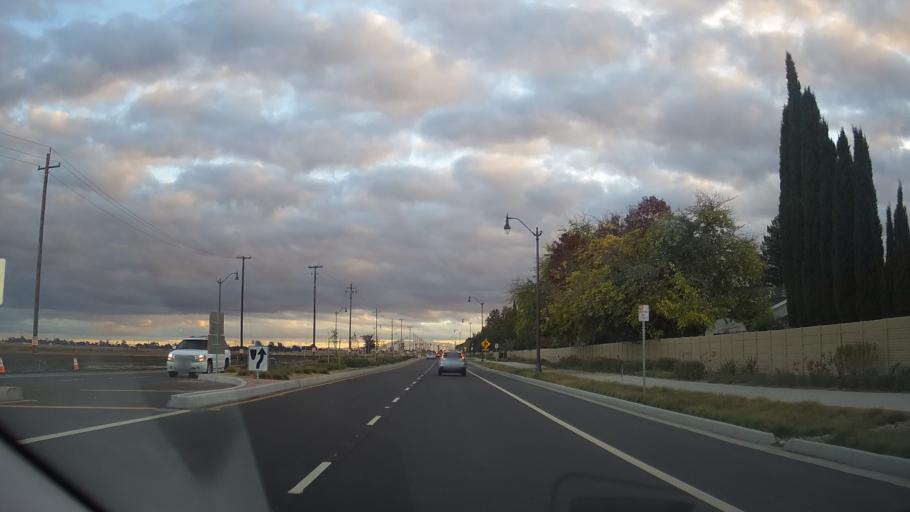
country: US
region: California
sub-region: Solano County
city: Vacaville
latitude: 38.3473
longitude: -121.9340
